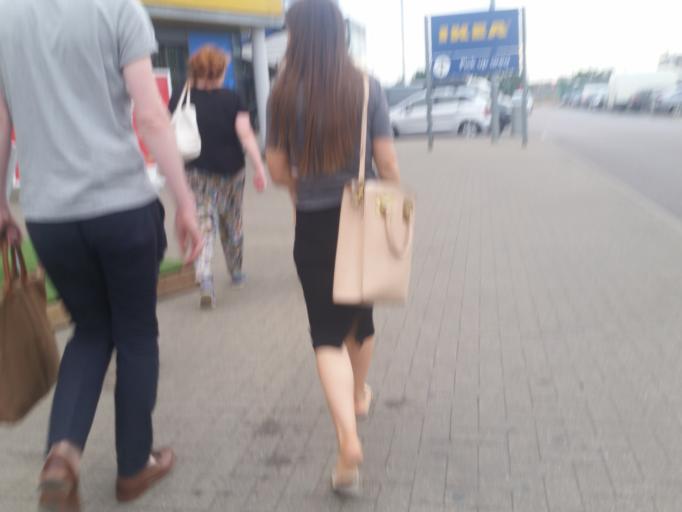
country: GB
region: England
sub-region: Greater London
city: Walthamstow
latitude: 51.6088
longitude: -0.0463
